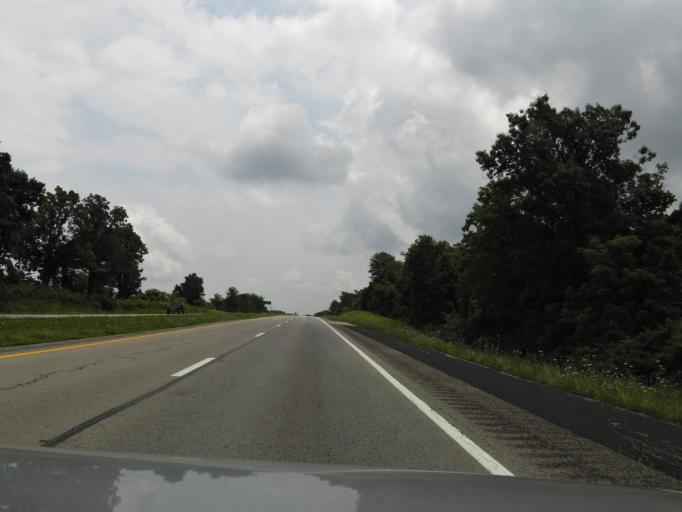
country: US
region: Kentucky
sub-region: Grayson County
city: Leitchfield
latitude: 37.5513
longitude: -86.1039
